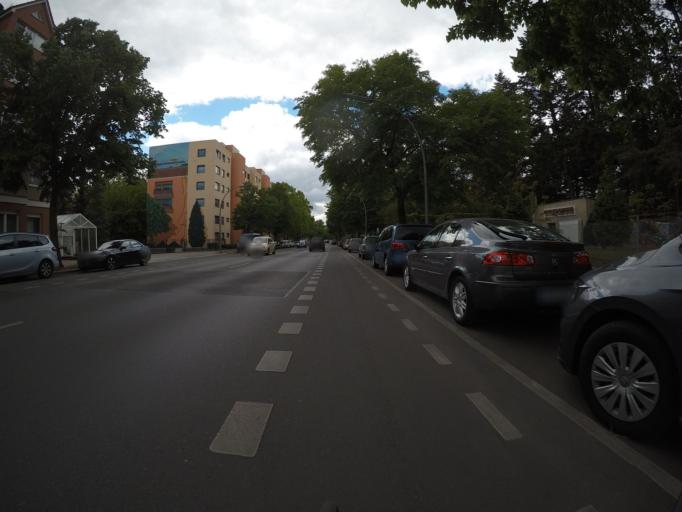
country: DE
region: Berlin
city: Wedding Bezirk
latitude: 52.5601
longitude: 13.3537
